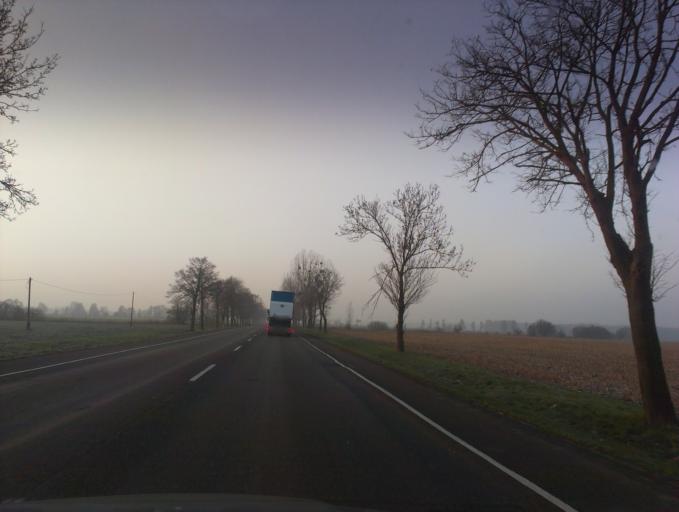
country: PL
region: Greater Poland Voivodeship
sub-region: Powiat obornicki
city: Rogozno
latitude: 52.7549
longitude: 16.9609
